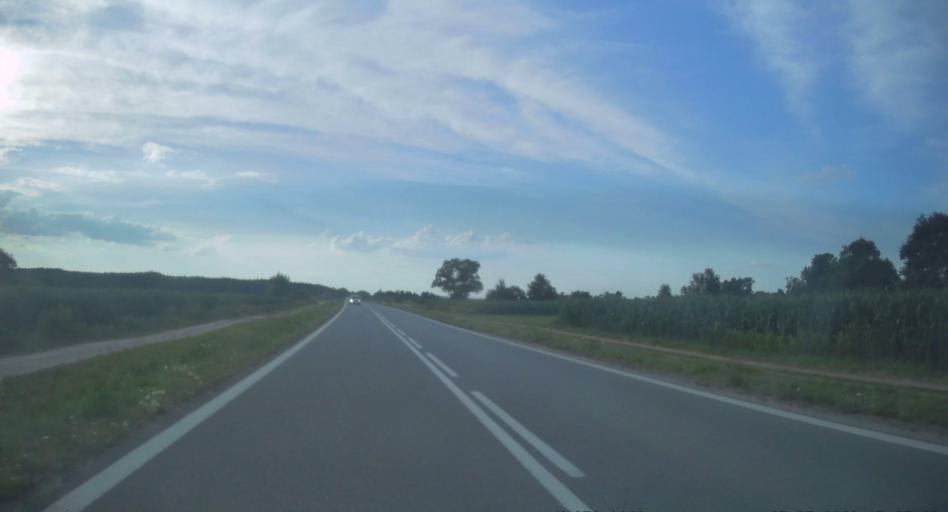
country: PL
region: Lesser Poland Voivodeship
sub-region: Powiat brzeski
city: Szczurowa
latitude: 50.0863
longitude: 20.6305
